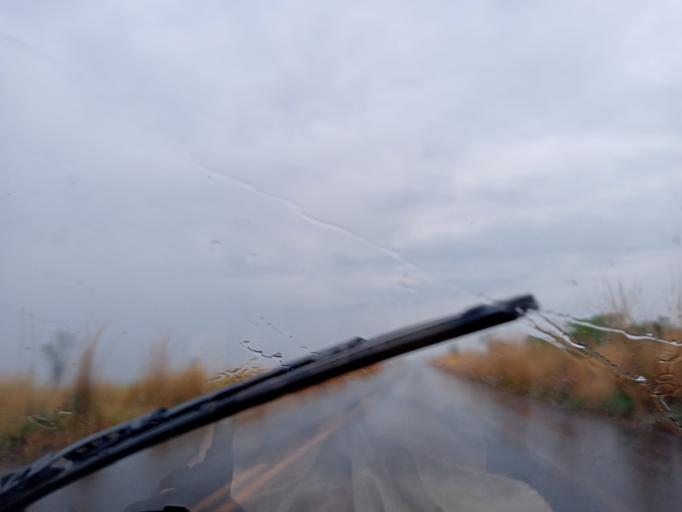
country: BR
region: Minas Gerais
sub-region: Ituiutaba
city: Ituiutaba
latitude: -19.0813
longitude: -49.5066
